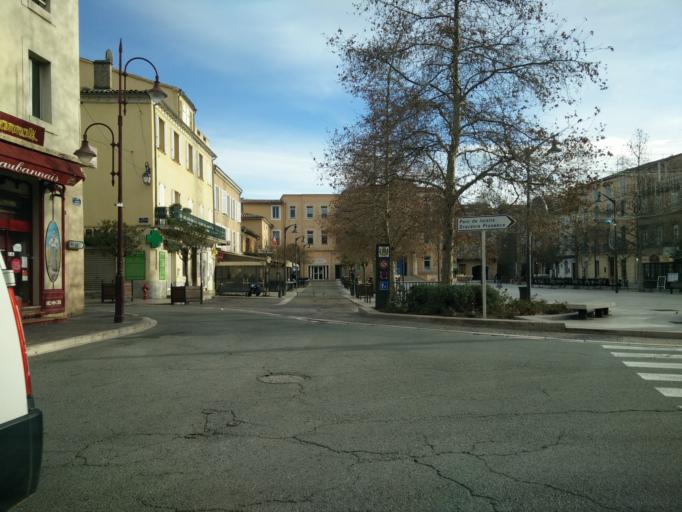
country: FR
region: Provence-Alpes-Cote d'Azur
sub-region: Departement du Var
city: Vidauban
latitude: 43.4273
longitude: 6.4311
